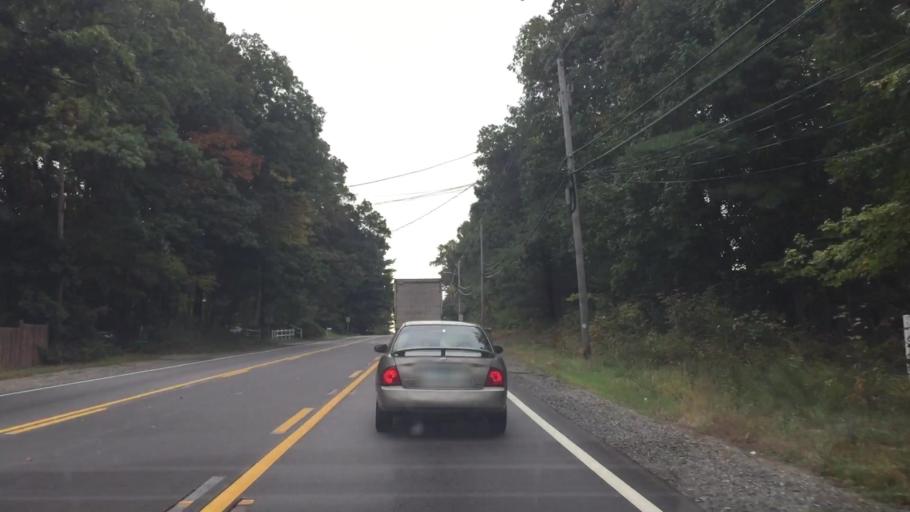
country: US
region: Massachusetts
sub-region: Middlesex County
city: North Reading
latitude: 42.6277
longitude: -71.0626
